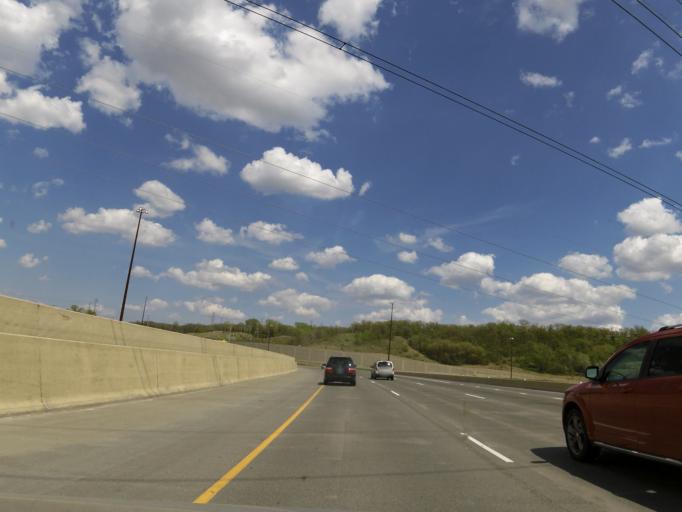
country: US
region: Minnesota
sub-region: Washington County
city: Newport
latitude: 44.8852
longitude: -93.0061
